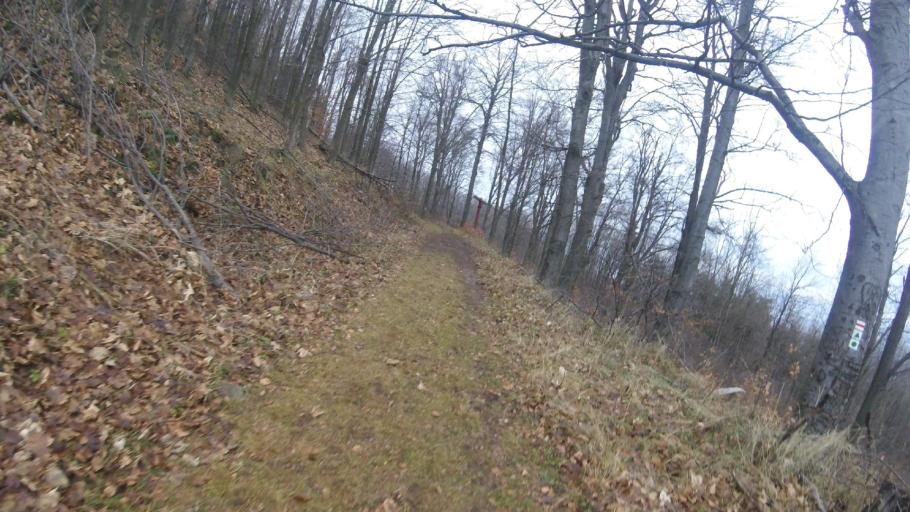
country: HU
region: Heves
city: Paradsasvar
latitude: 47.9184
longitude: 19.9253
